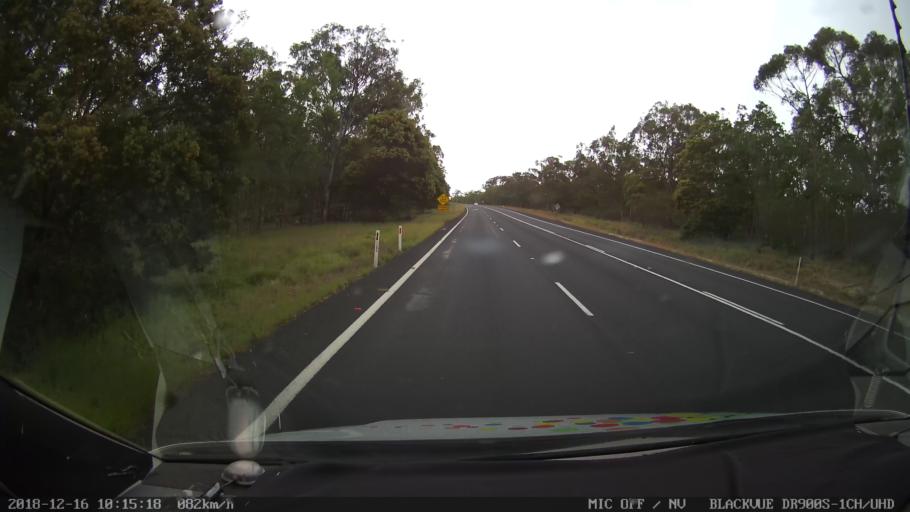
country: AU
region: New South Wales
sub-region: Tenterfield Municipality
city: Carrolls Creek
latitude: -29.2786
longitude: 151.9715
